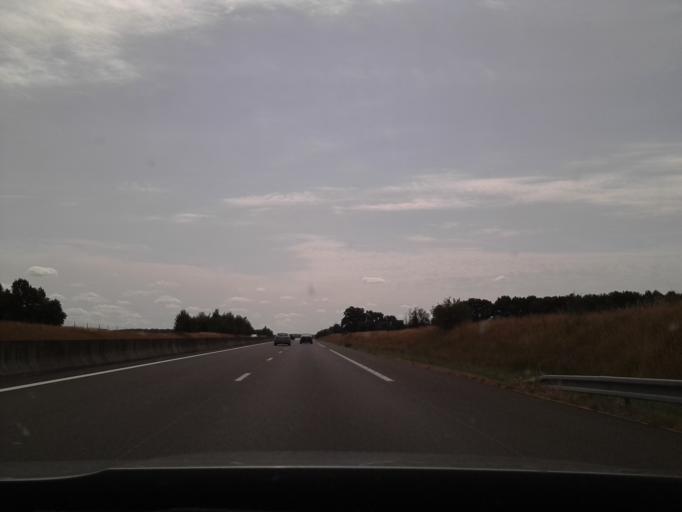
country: FR
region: Centre
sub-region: Departement d'Indre-et-Loire
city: Saint-Paterne-Racan
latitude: 47.6205
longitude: 0.5174
